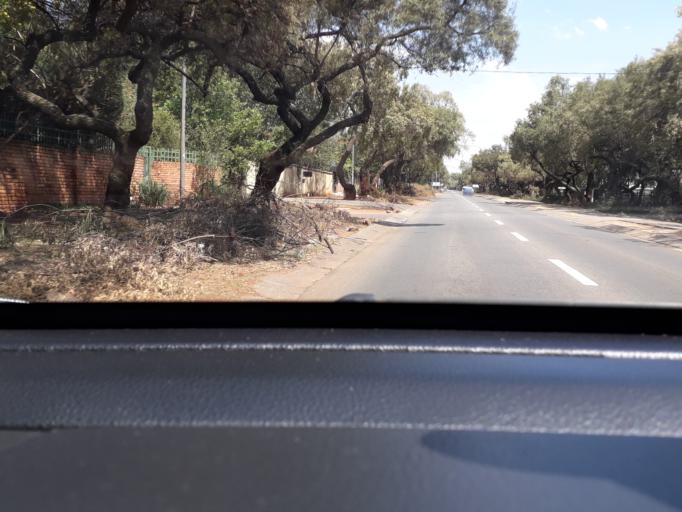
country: ZA
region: Gauteng
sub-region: City of Tshwane Metropolitan Municipality
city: Centurion
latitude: -25.8206
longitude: 28.2065
